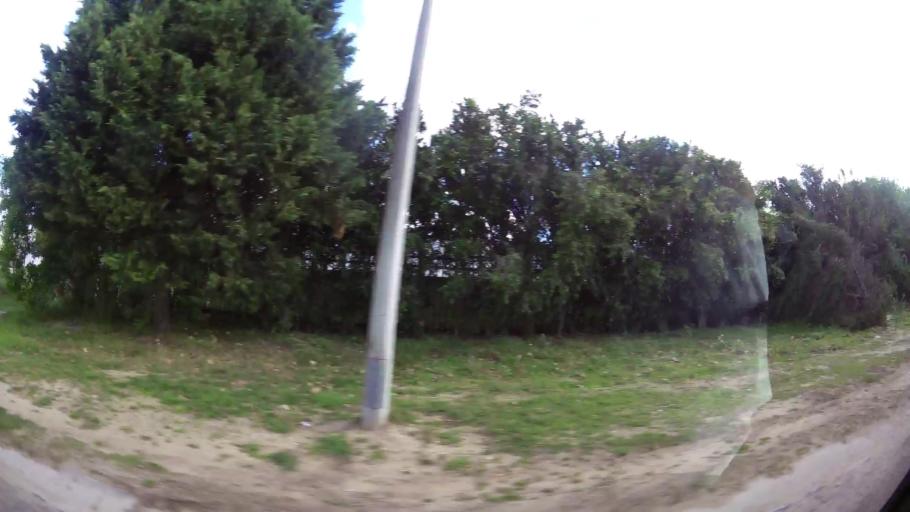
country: ZA
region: Western Cape
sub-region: Eden District Municipality
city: Knysna
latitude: -34.0459
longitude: 23.0799
